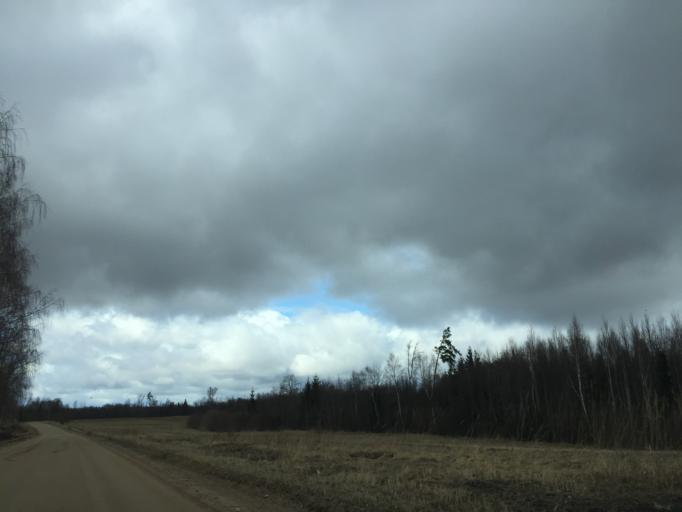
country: LV
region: Ilukste
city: Ilukste
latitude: 56.0778
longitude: 26.0399
